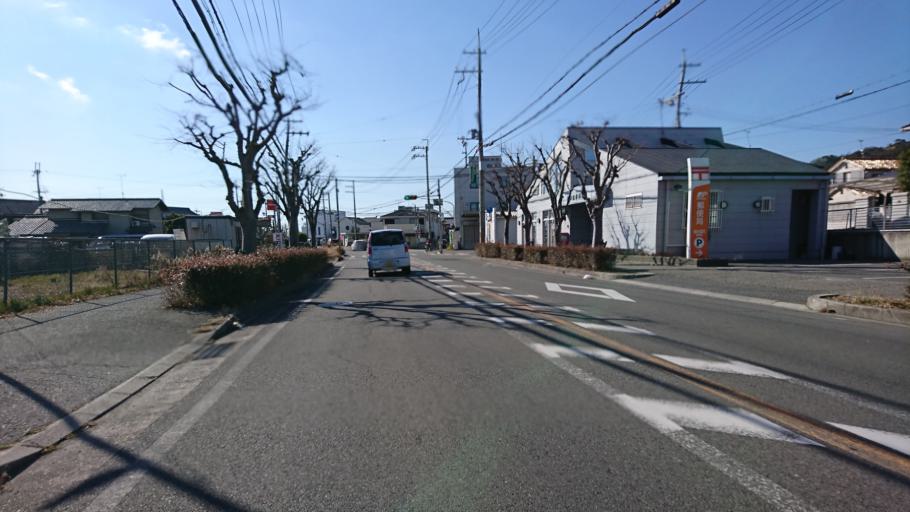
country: JP
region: Hyogo
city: Kakogawacho-honmachi
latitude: 34.7765
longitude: 134.8046
